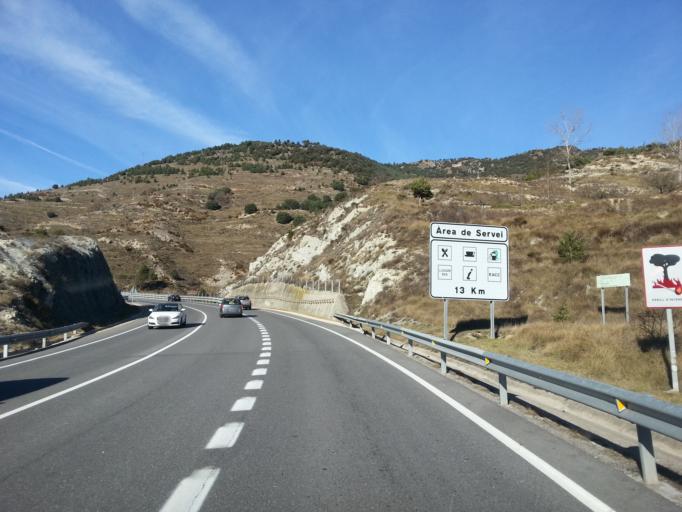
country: ES
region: Catalonia
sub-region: Provincia de Barcelona
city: Baga
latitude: 42.2569
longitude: 1.8653
